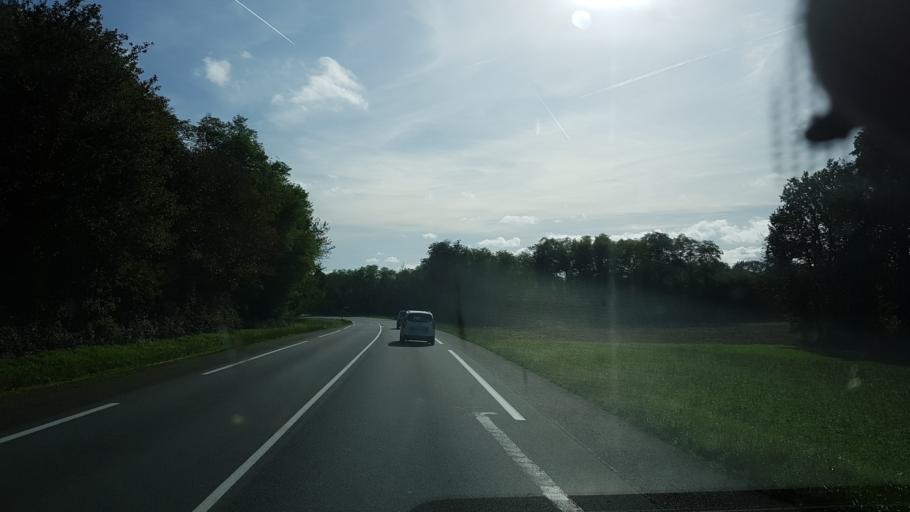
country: FR
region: Poitou-Charentes
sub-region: Departement de la Charente
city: Saint-Claud
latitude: 45.8688
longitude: 0.4661
